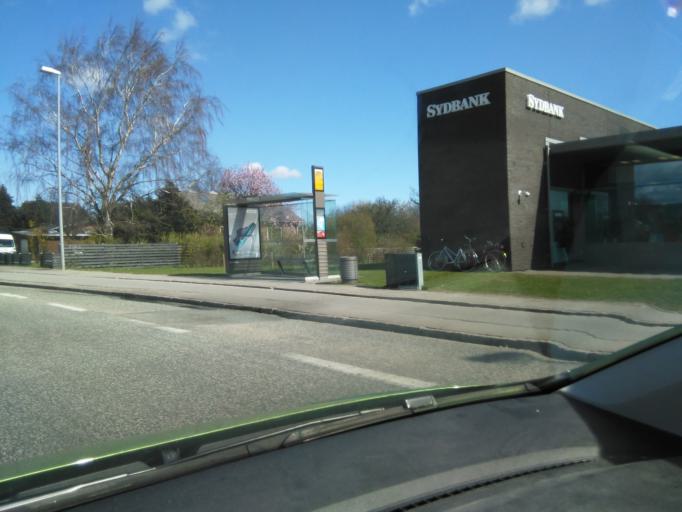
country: DK
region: Central Jutland
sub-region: Arhus Kommune
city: Lystrup
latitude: 56.2003
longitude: 10.2374
